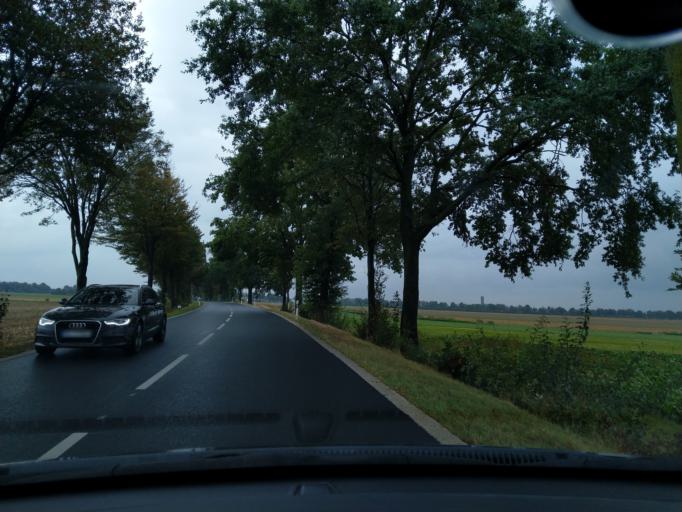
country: DE
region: North Rhine-Westphalia
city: Erkelenz
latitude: 51.0890
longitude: 6.2766
